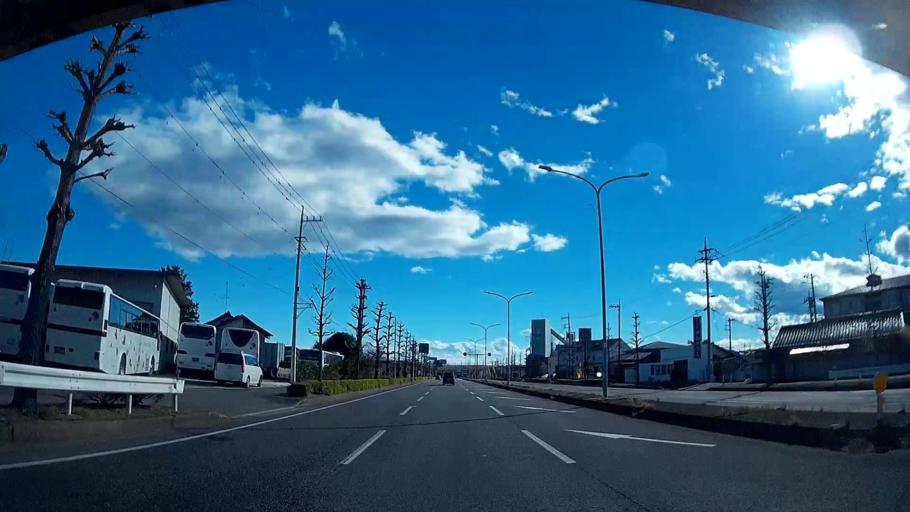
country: JP
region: Saitama
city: Yorii
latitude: 36.1241
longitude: 139.2048
